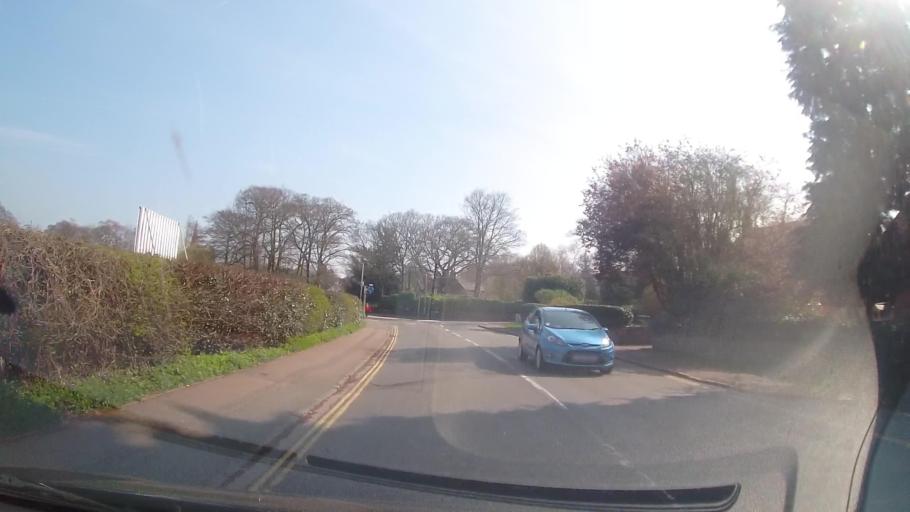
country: GB
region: England
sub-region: Leicestershire
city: Markfield
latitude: 52.6836
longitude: -1.2315
